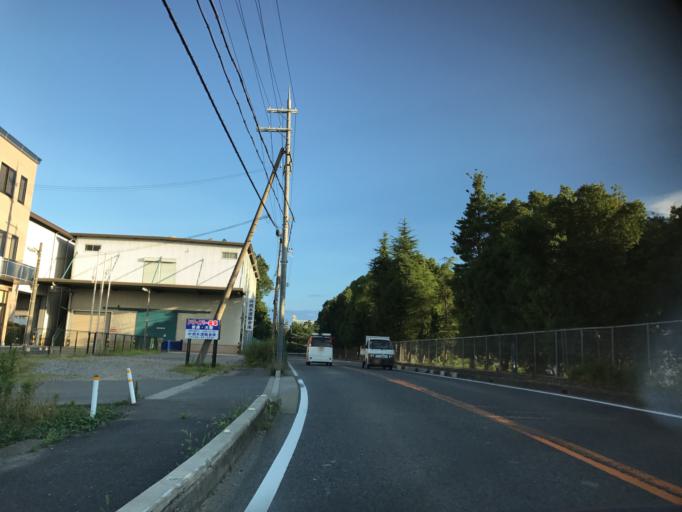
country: JP
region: Shiga Prefecture
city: Hino
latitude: 35.0335
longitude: 136.2443
